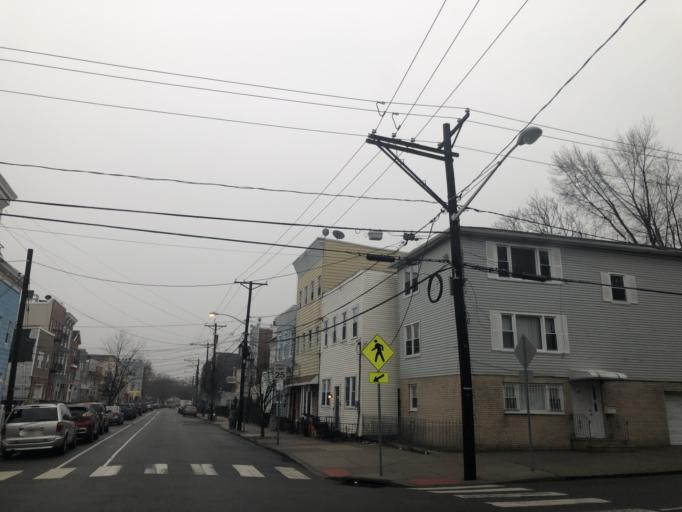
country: US
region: New Jersey
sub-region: Hudson County
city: Hoboken
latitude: 40.7453
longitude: -74.0476
